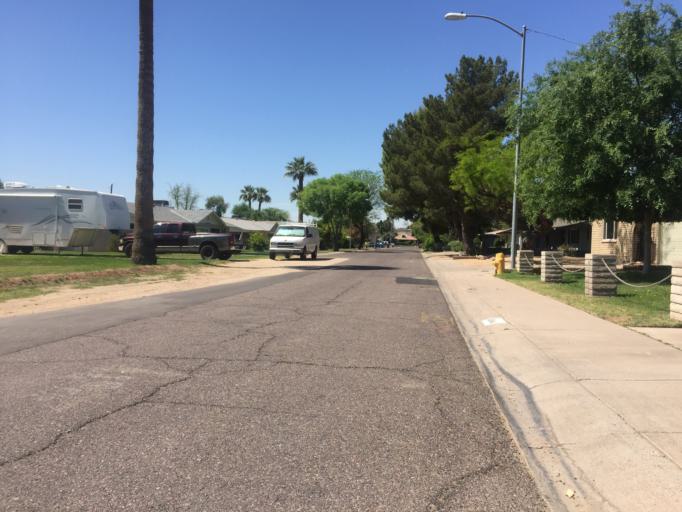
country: US
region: Arizona
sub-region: Maricopa County
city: Phoenix
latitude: 33.5320
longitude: -112.0624
